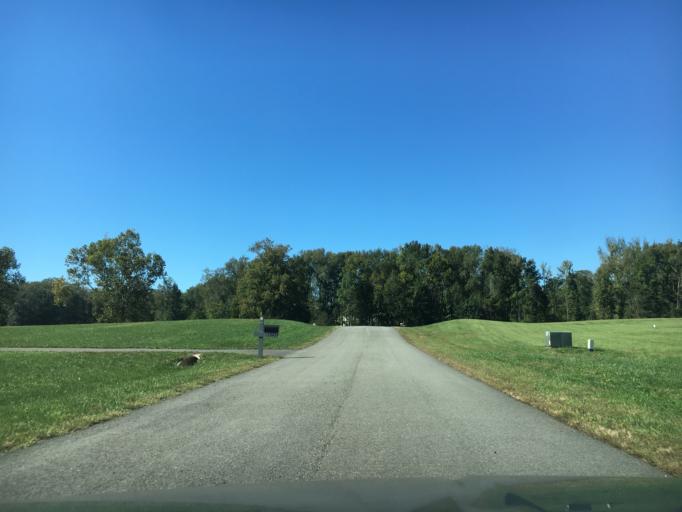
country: US
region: Virginia
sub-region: Goochland County
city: Goochland
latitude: 37.6947
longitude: -77.8369
